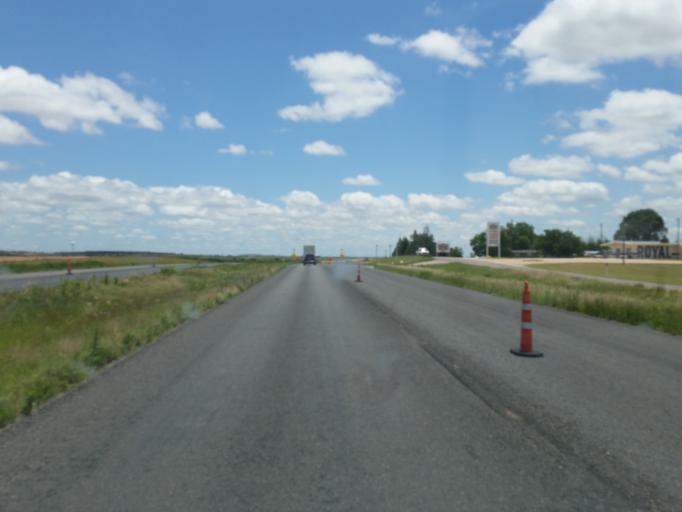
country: US
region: Texas
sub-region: Scurry County
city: Snyder
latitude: 32.7245
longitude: -100.8901
